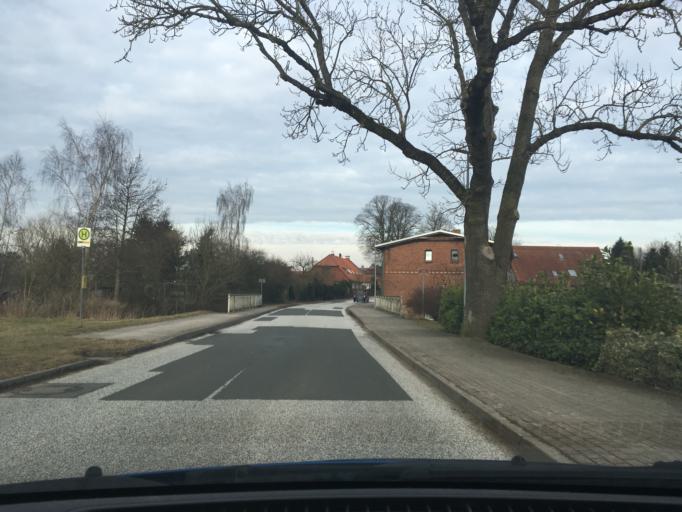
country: DE
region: Mecklenburg-Vorpommern
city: Stralendorf
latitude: 53.5634
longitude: 11.2611
